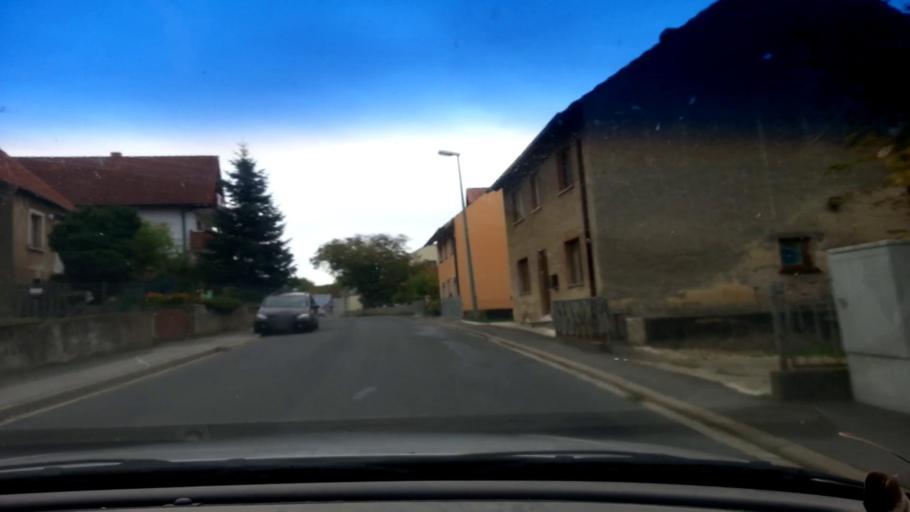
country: DE
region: Bavaria
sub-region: Upper Franconia
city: Priesendorf
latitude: 49.9077
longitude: 10.7076
